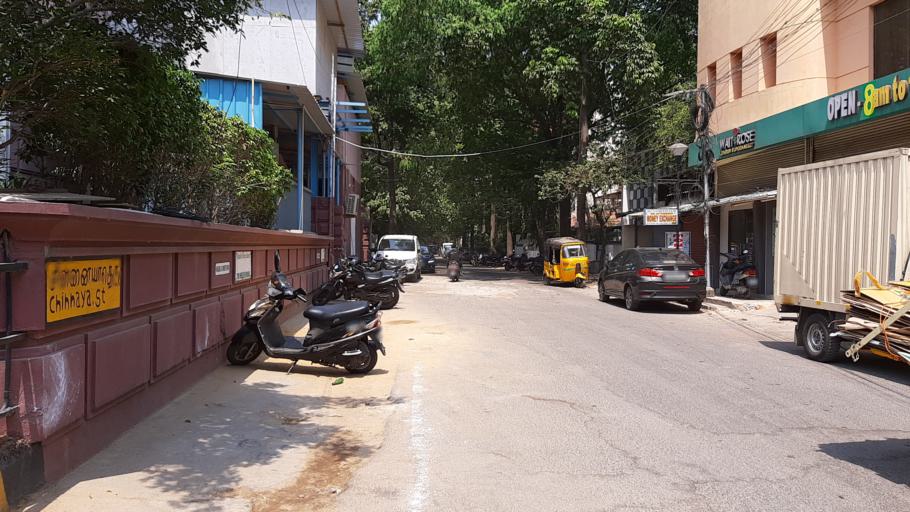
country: IN
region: Tamil Nadu
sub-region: Chennai
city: Chetput
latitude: 13.0475
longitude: 80.2398
